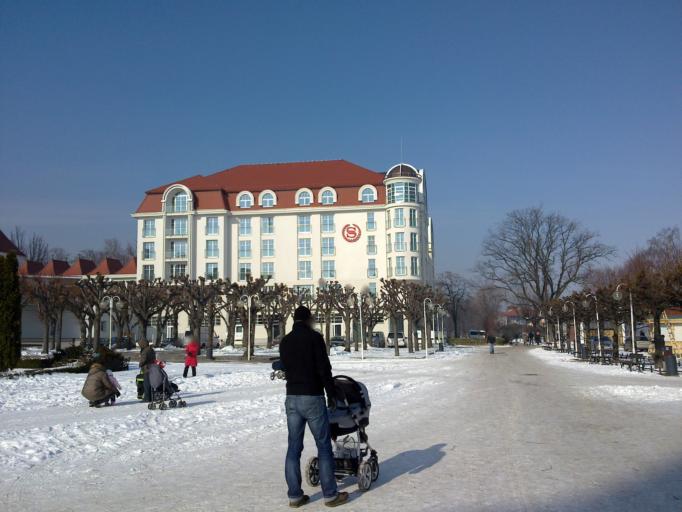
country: PL
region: Pomeranian Voivodeship
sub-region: Sopot
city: Sopot
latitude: 54.4456
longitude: 18.5698
